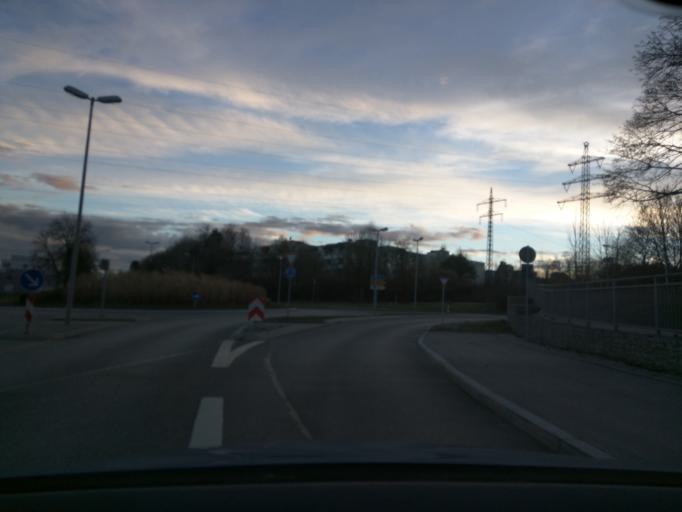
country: DE
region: Bavaria
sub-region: Upper Bavaria
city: Freising
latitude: 48.4133
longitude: 11.7478
